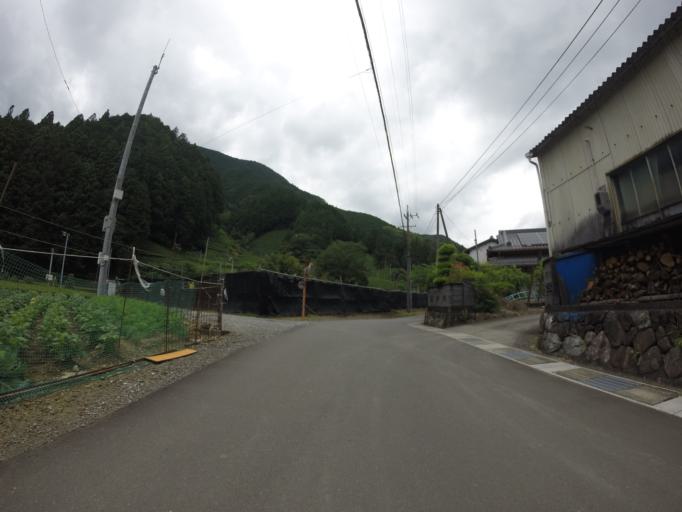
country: JP
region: Shizuoka
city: Shizuoka-shi
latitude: 35.0138
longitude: 138.3080
